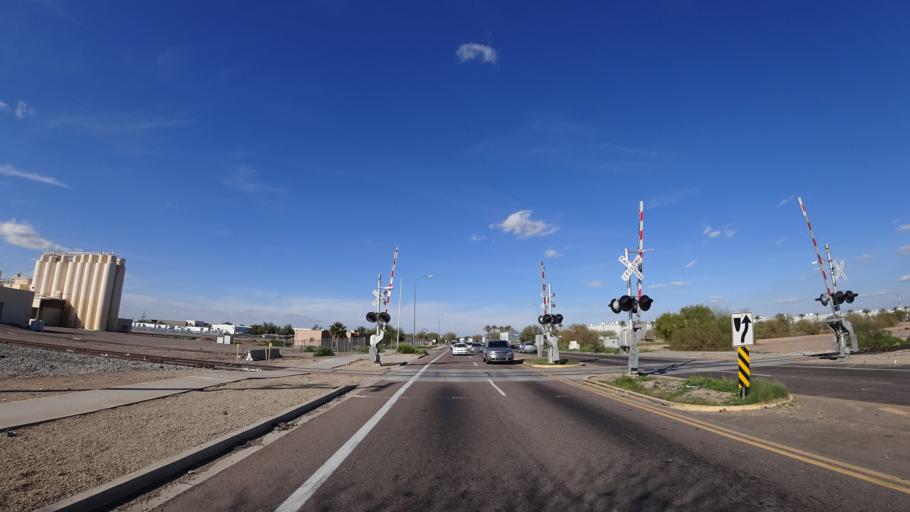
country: US
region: Arizona
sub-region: Maricopa County
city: Tolleson
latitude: 33.4444
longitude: -112.2213
